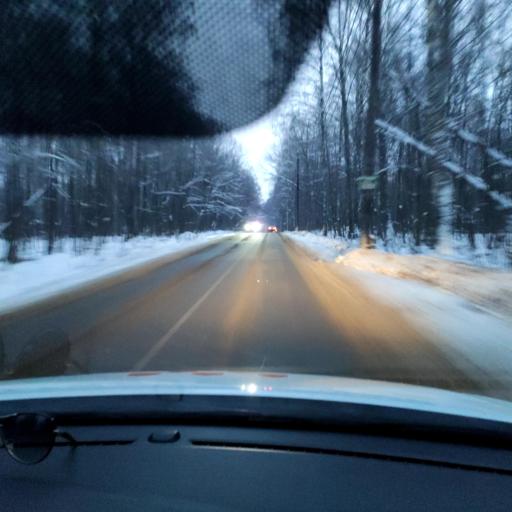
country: RU
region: Tatarstan
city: Vysokaya Gora
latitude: 55.9330
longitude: 49.1845
